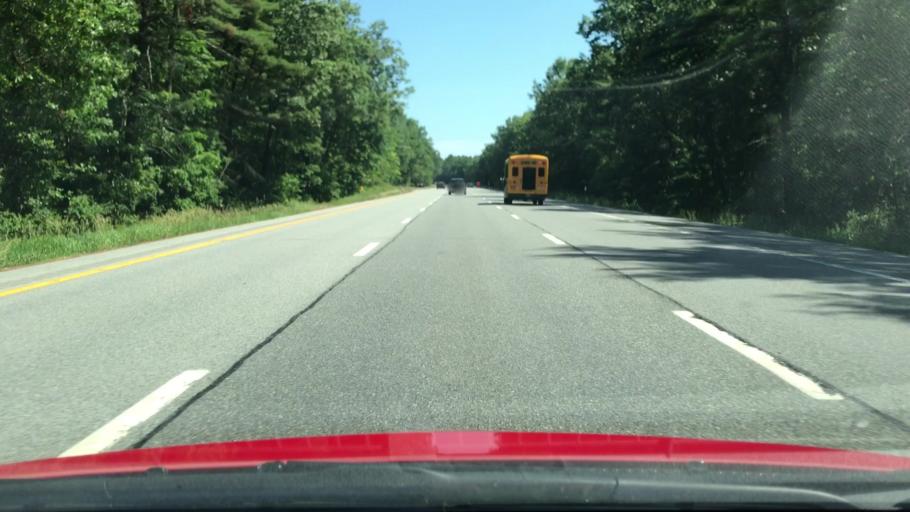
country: US
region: New York
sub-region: Warren County
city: West Glens Falls
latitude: 43.2469
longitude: -73.6876
